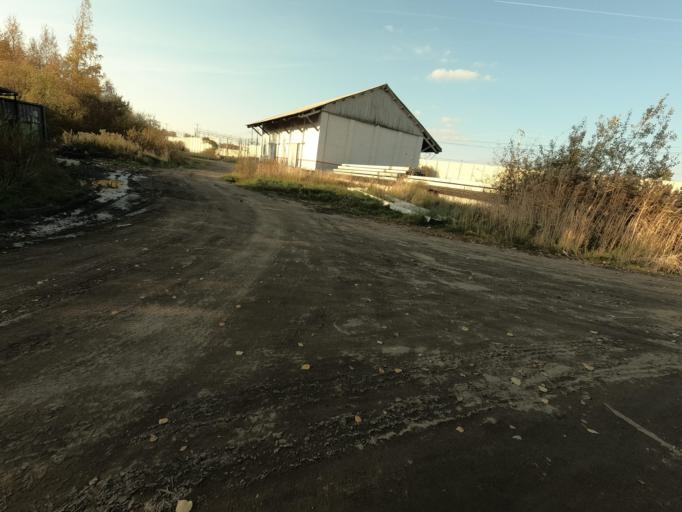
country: RU
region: Leningrad
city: Mga
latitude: 59.7551
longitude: 31.0558
